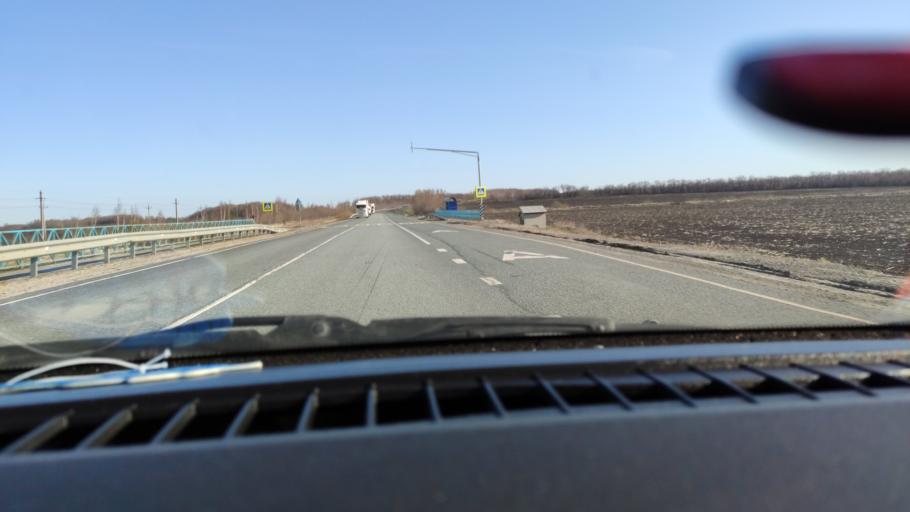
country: RU
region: Samara
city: Syzran'
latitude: 52.9707
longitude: 48.3083
